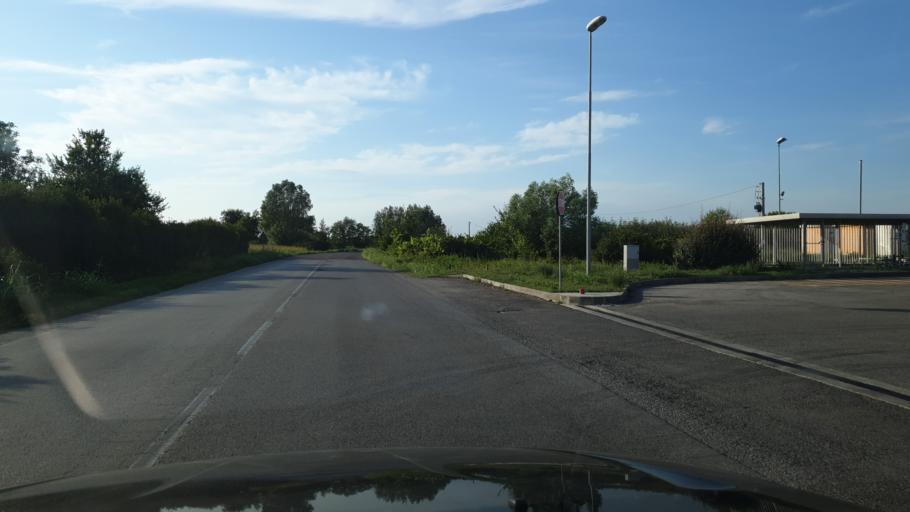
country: IT
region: Veneto
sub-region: Provincia di Rovigo
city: Fiesso Umbertiano
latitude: 44.9534
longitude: 11.6177
